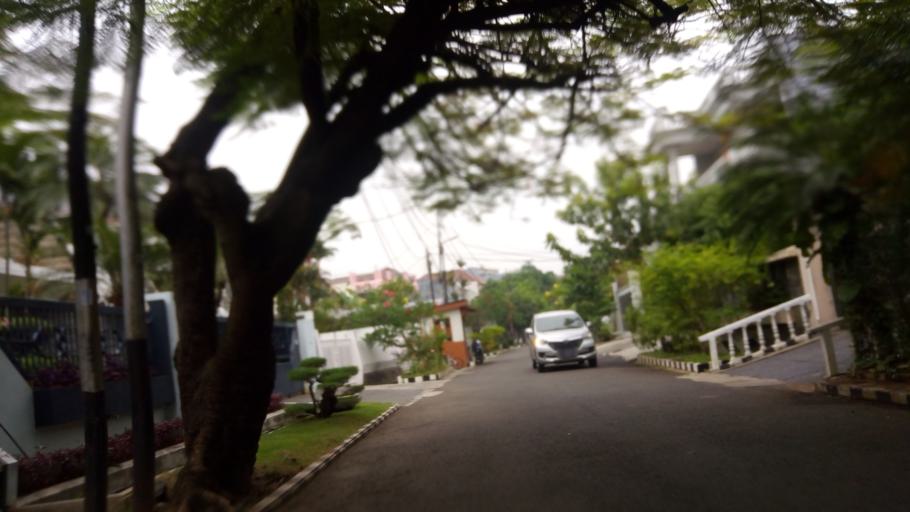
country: ID
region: Jakarta Raya
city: Jakarta
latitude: -6.1453
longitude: 106.8428
